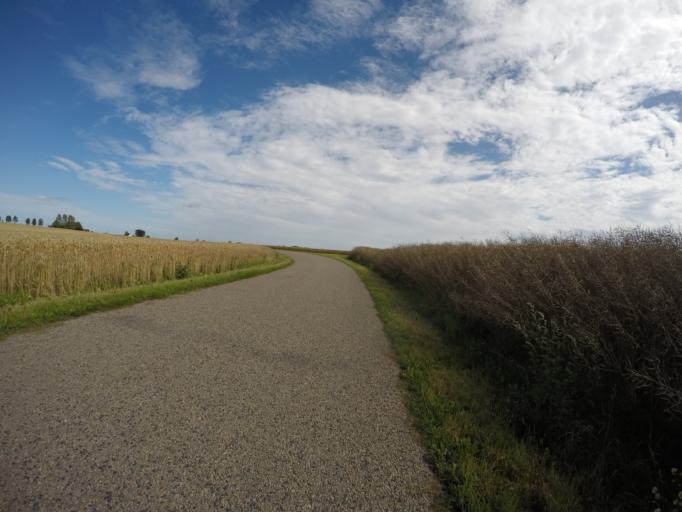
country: SE
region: Skane
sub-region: Simrishamns Kommun
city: Simrishamn
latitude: 55.4931
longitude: 14.2479
